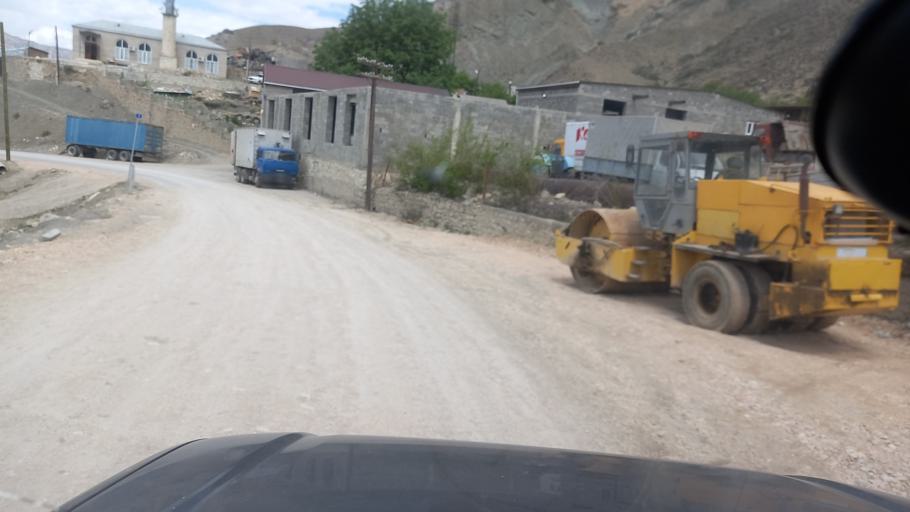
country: RU
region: Dagestan
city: Gunib
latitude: 42.3665
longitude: 46.9711
